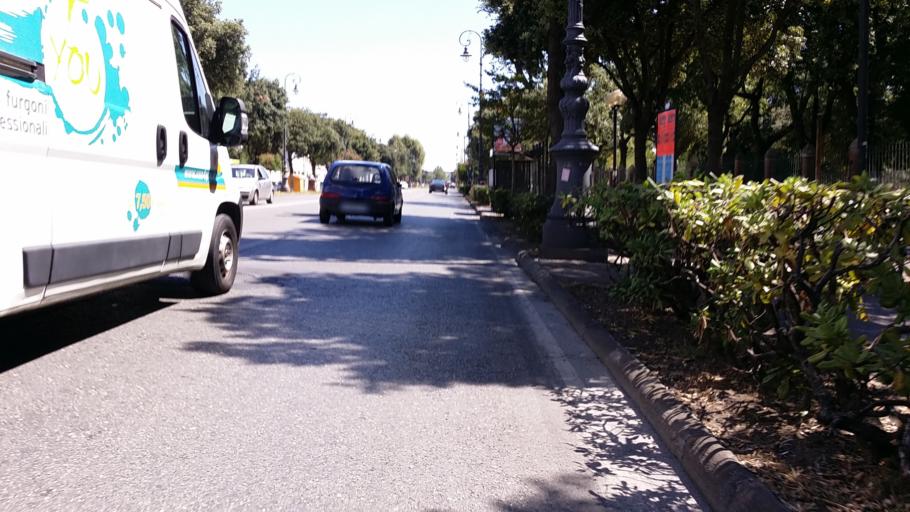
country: IT
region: Tuscany
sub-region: Provincia di Livorno
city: Livorno
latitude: 43.5530
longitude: 10.3201
